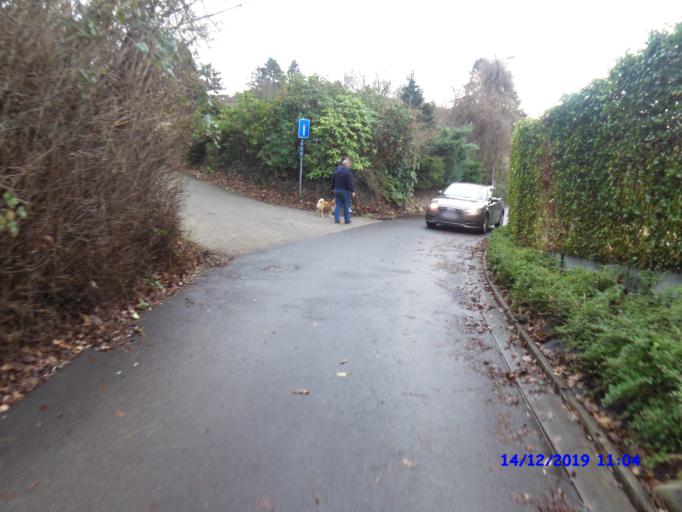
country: BE
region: Flanders
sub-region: Provincie Vlaams-Brabant
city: Beersel
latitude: 50.7569
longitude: 4.3037
